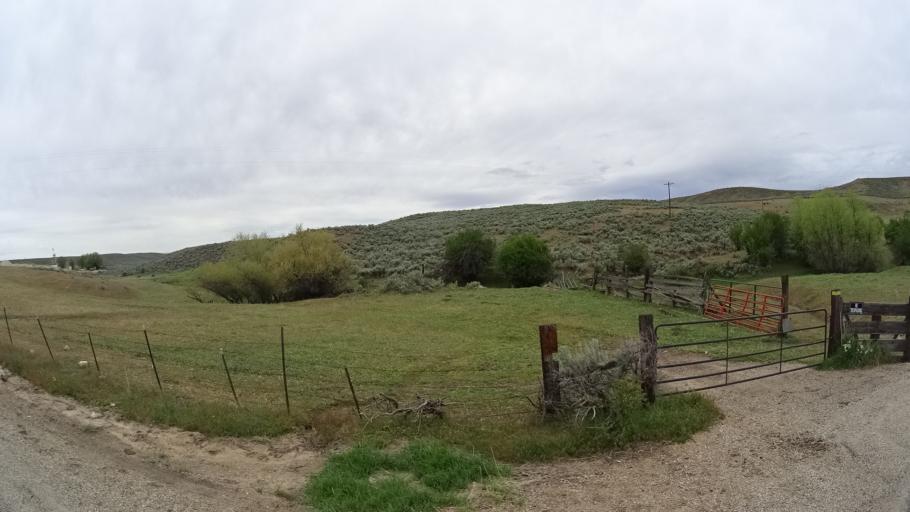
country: US
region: Idaho
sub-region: Ada County
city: Boise
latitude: 43.4818
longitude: -115.9983
